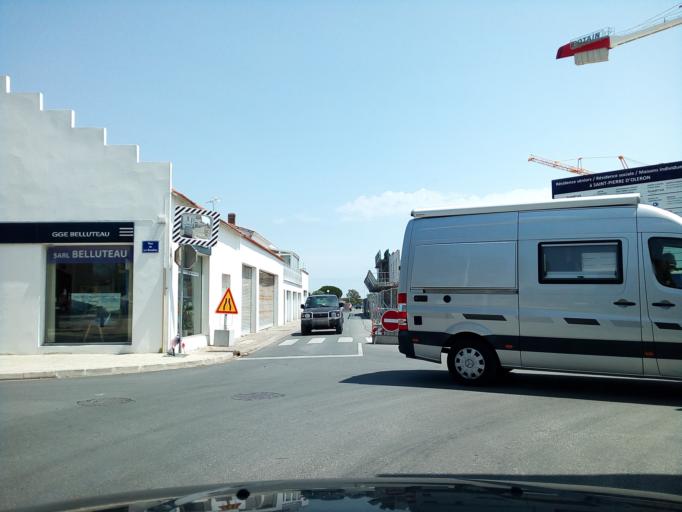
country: FR
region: Poitou-Charentes
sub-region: Departement de la Charente-Maritime
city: Dolus-d'Oleron
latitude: 45.9409
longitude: -1.3074
